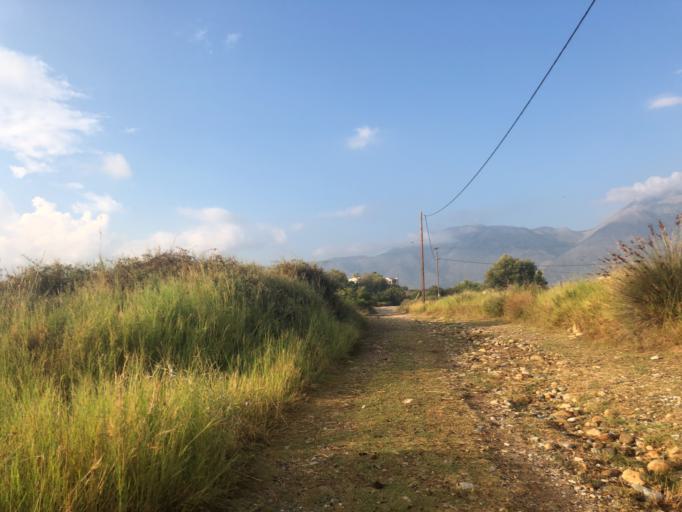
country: GR
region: Crete
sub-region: Nomos Chanias
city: Georgioupolis
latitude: 35.3516
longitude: 24.3088
